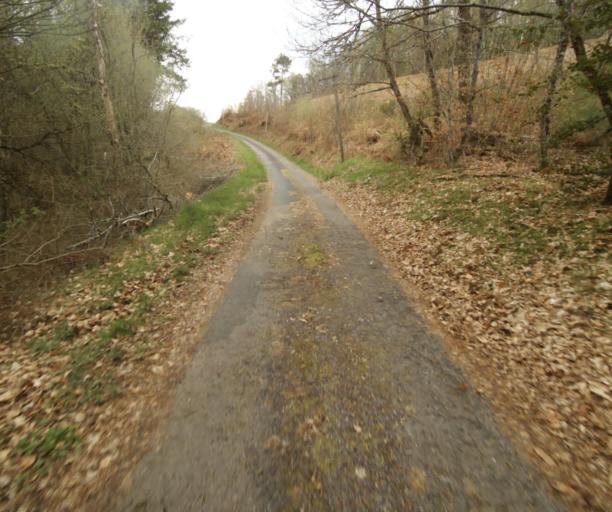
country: FR
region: Limousin
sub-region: Departement de la Correze
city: Laguenne
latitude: 45.2485
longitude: 1.8684
